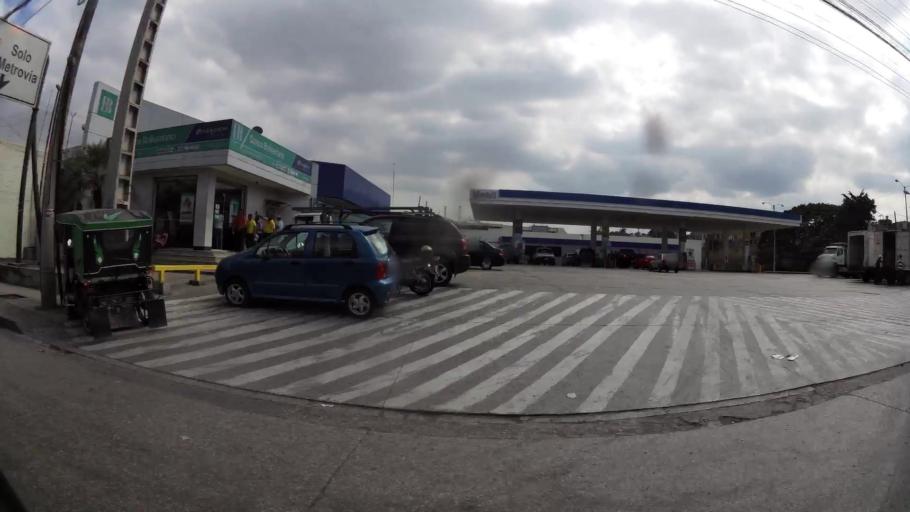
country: EC
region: Guayas
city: Santa Lucia
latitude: -2.0919
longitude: -79.9370
